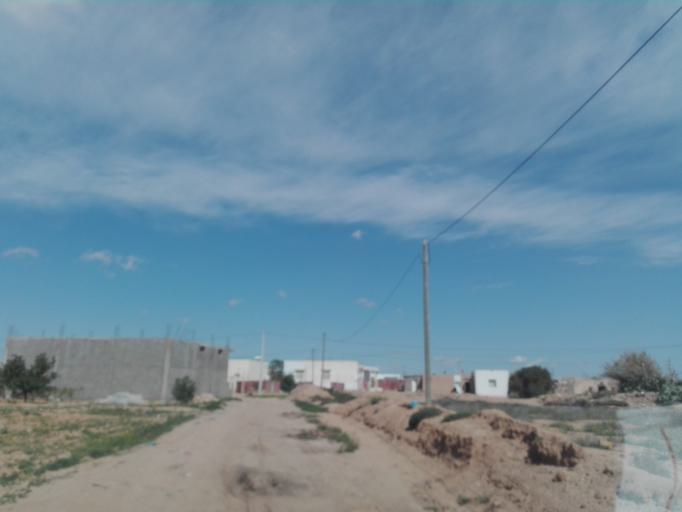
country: TN
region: Safaqis
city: Sfax
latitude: 34.7315
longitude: 10.5084
